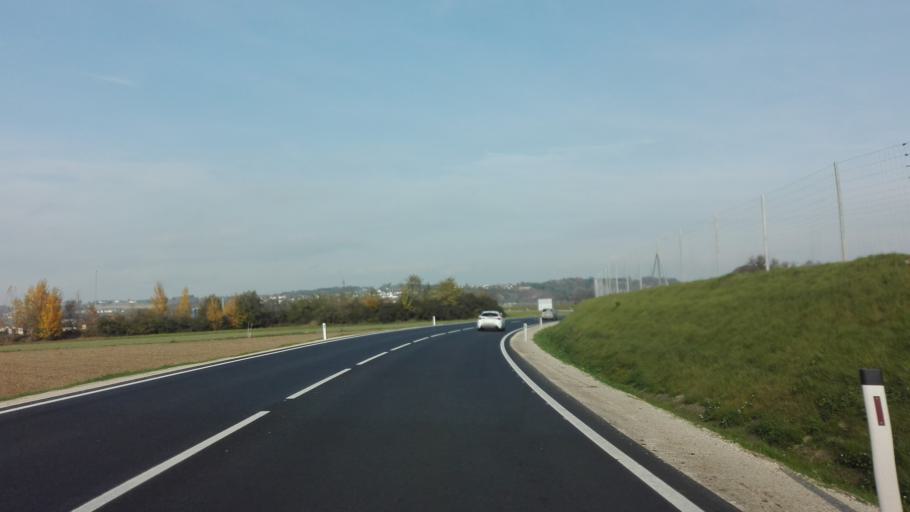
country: AT
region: Lower Austria
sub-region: Politischer Bezirk Amstetten
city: Ennsdorf
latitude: 48.2231
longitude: 14.5115
